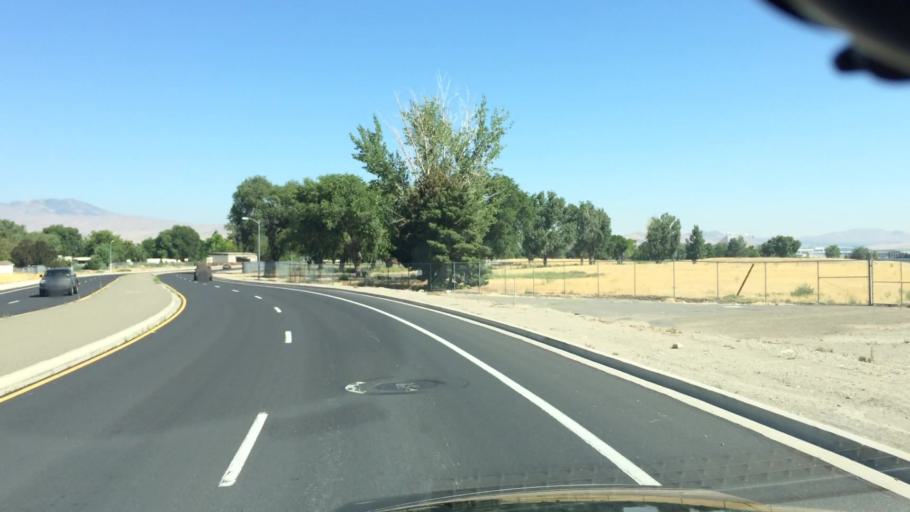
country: US
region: Nevada
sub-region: Washoe County
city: Sparks
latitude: 39.4831
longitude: -119.7733
